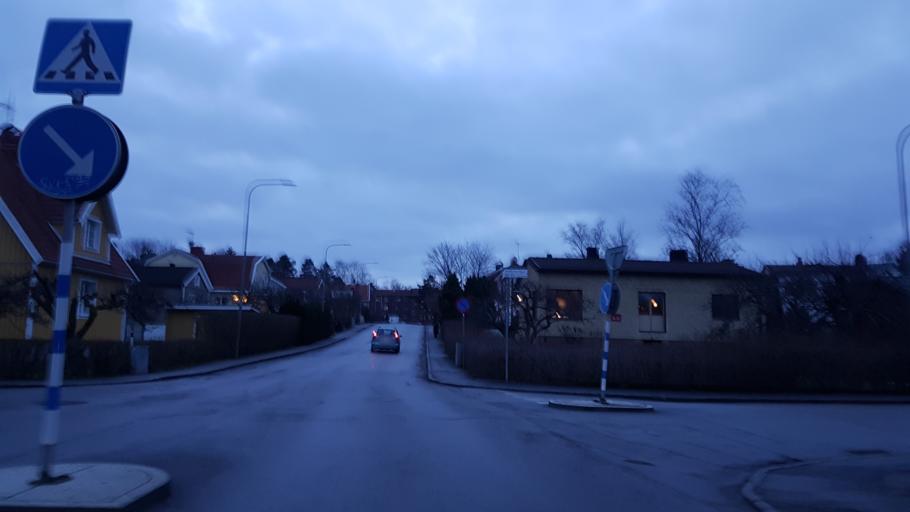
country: SE
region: Stockholm
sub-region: Stockholms Kommun
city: Arsta
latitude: 59.2794
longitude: 18.0490
